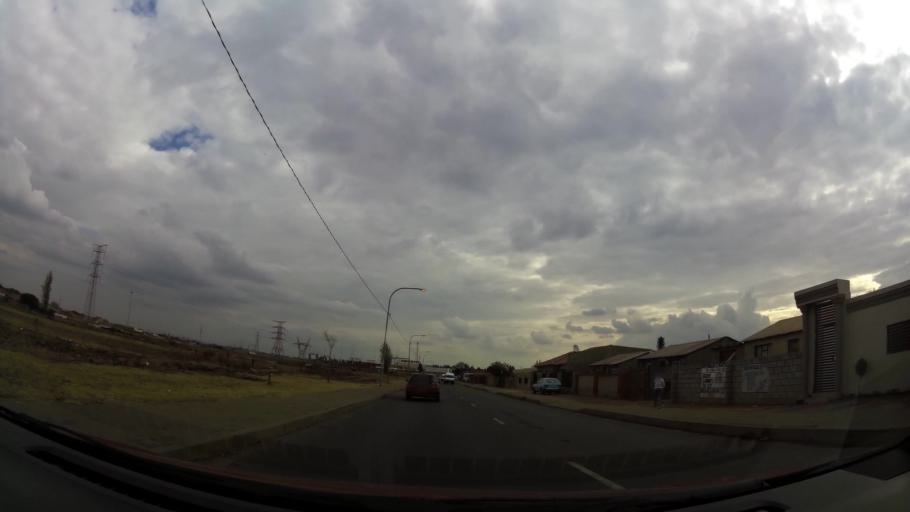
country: ZA
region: Gauteng
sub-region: City of Johannesburg Metropolitan Municipality
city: Soweto
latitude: -26.2403
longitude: 27.8504
